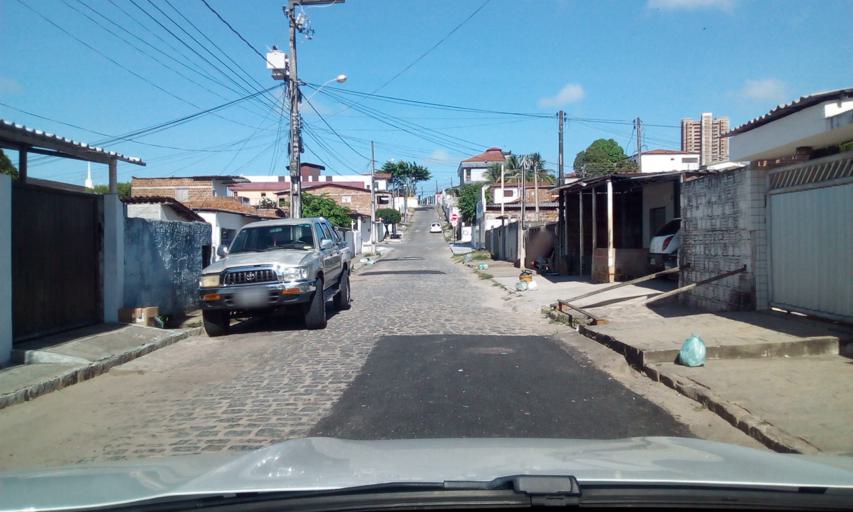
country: BR
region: Paraiba
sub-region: Joao Pessoa
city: Joao Pessoa
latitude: -7.1038
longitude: -34.8605
